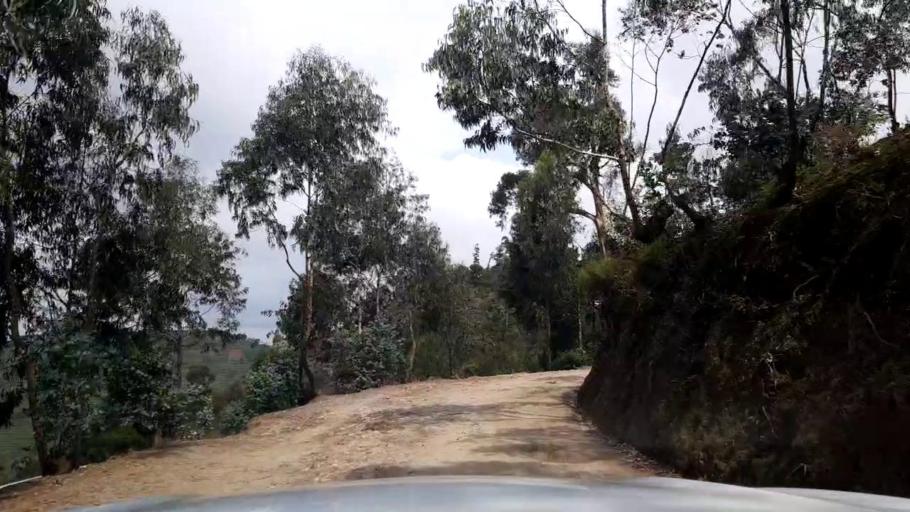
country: RW
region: Western Province
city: Kibuye
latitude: -1.9373
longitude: 29.4579
